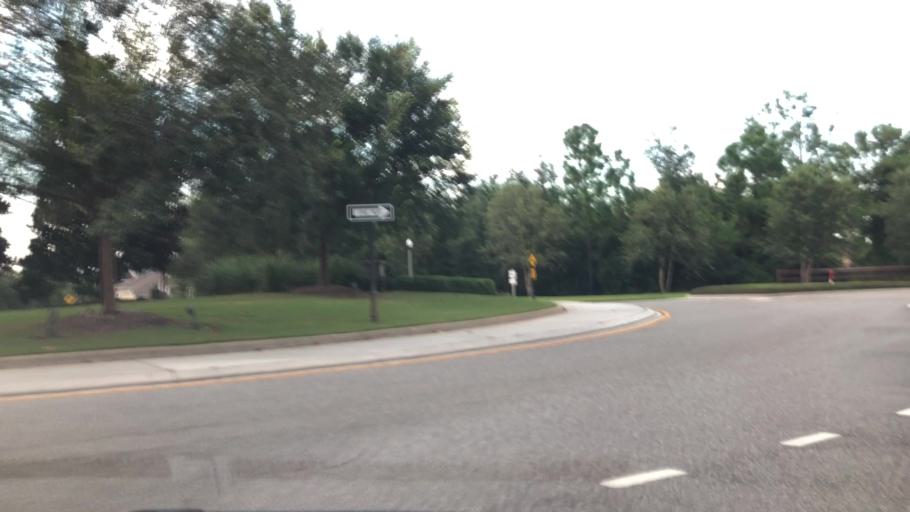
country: US
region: Florida
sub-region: Saint Johns County
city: Palm Valley
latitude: 30.0999
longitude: -81.4574
